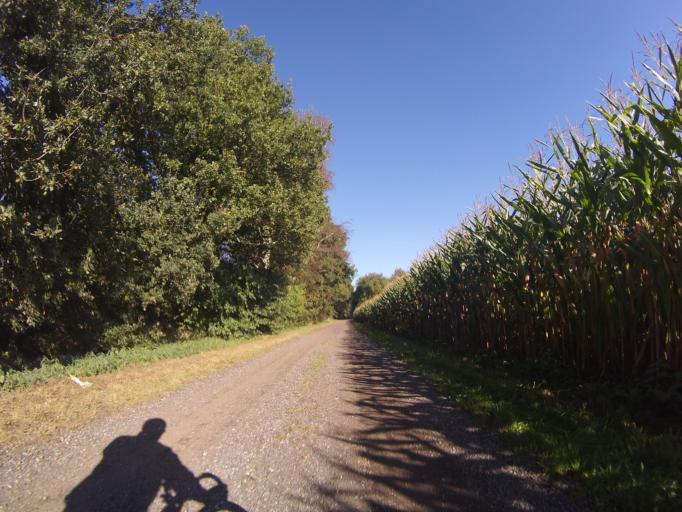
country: NL
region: Drenthe
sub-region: Gemeente Coevorden
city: Dalen
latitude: 52.7415
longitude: 6.6601
